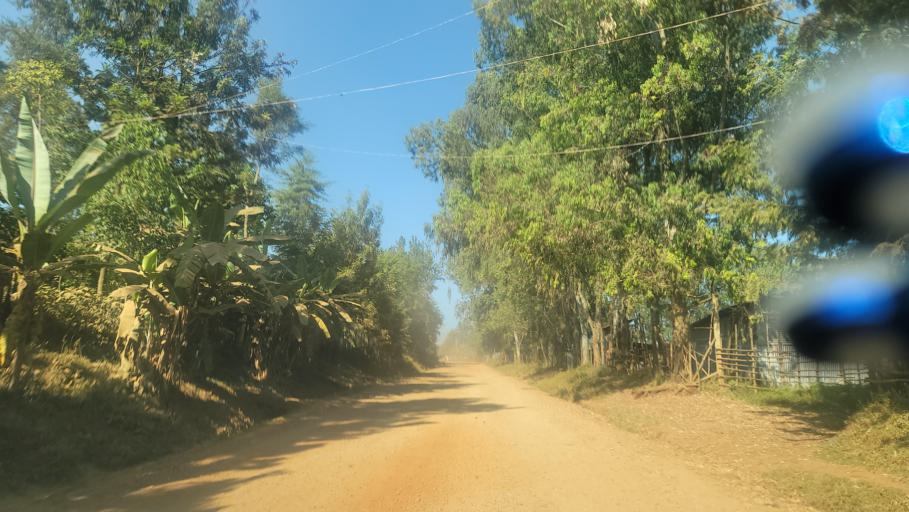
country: ET
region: Oromiya
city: Agaro
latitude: 7.8580
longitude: 36.5732
